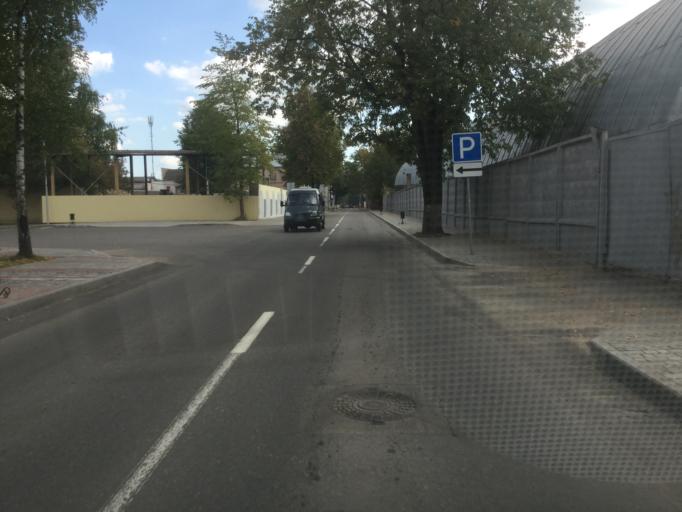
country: BY
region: Vitebsk
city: Vitebsk
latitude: 55.2000
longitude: 30.1905
